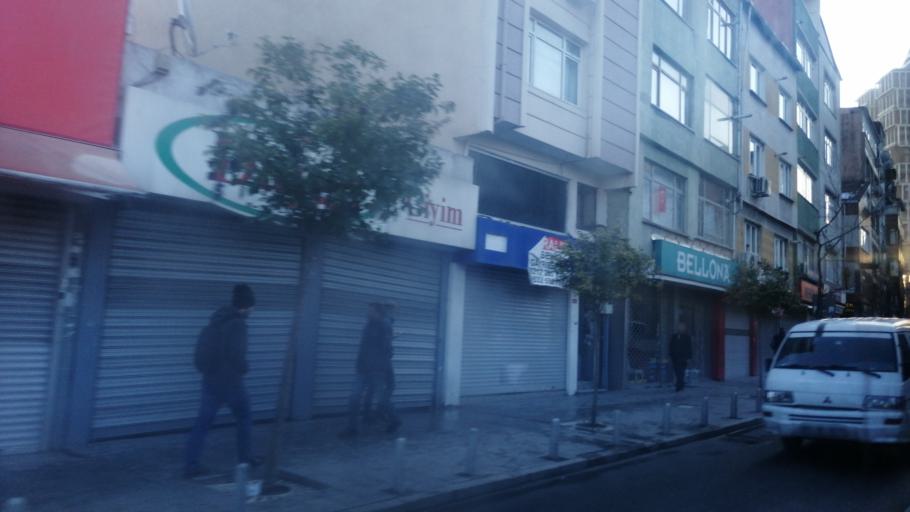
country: TR
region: Istanbul
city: Sisli
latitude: 41.0801
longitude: 28.9940
